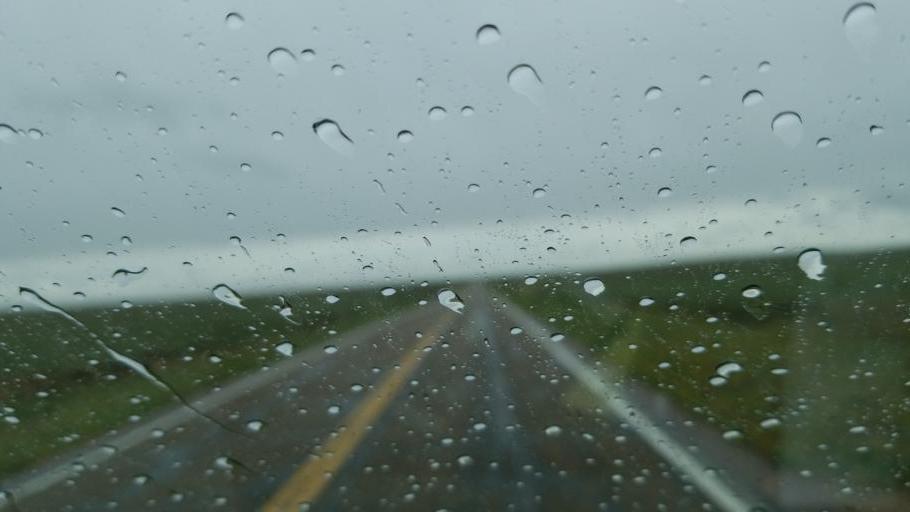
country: US
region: Colorado
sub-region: Lincoln County
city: Hugo
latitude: 38.8498
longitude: -103.2027
